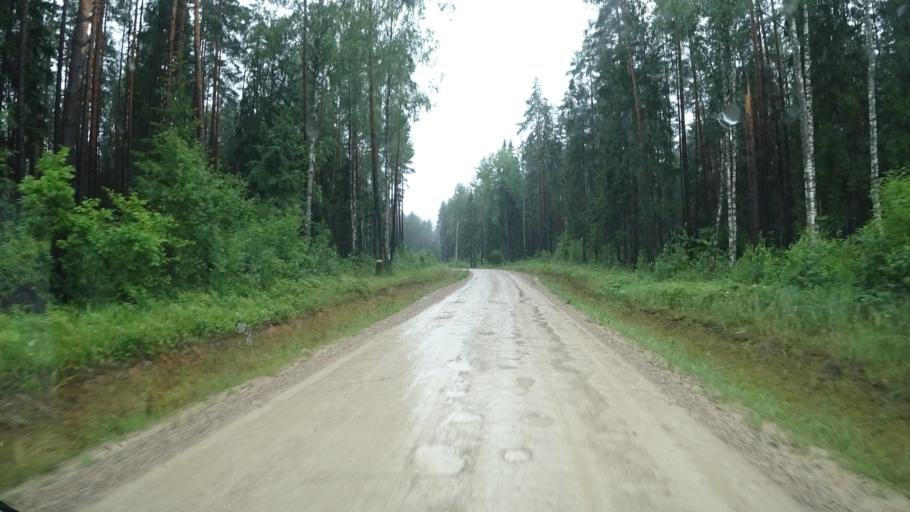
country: LV
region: Lecava
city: Iecava
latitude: 56.6571
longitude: 24.1749
